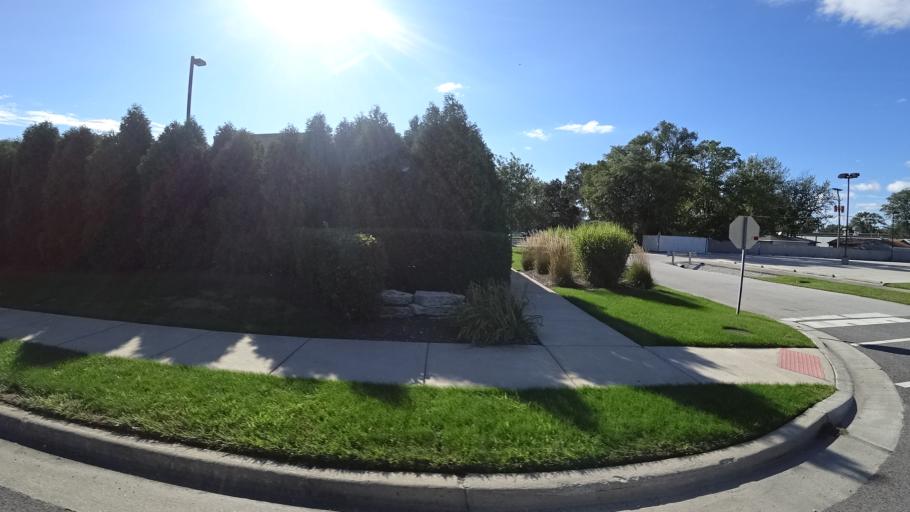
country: US
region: Illinois
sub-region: Cook County
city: Midlothian
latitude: 41.6307
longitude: -87.7376
